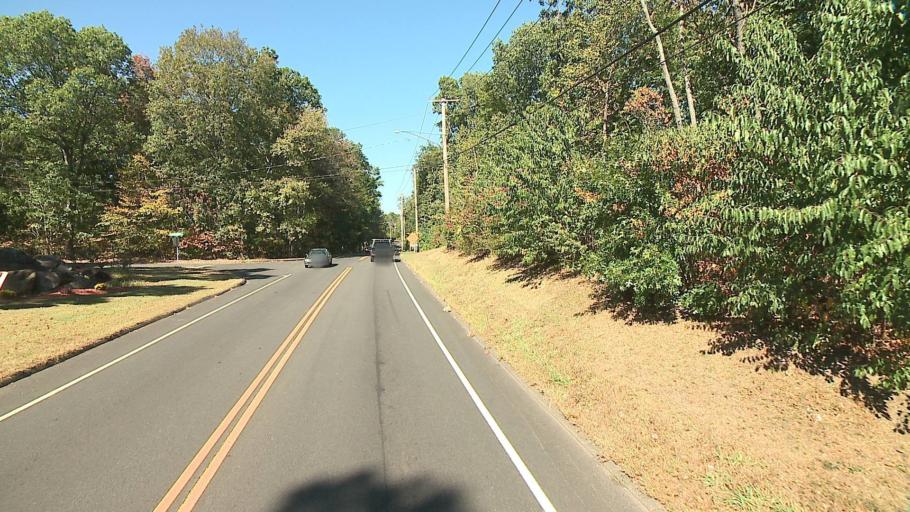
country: US
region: Connecticut
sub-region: New Haven County
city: Orange
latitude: 41.2928
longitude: -73.0151
